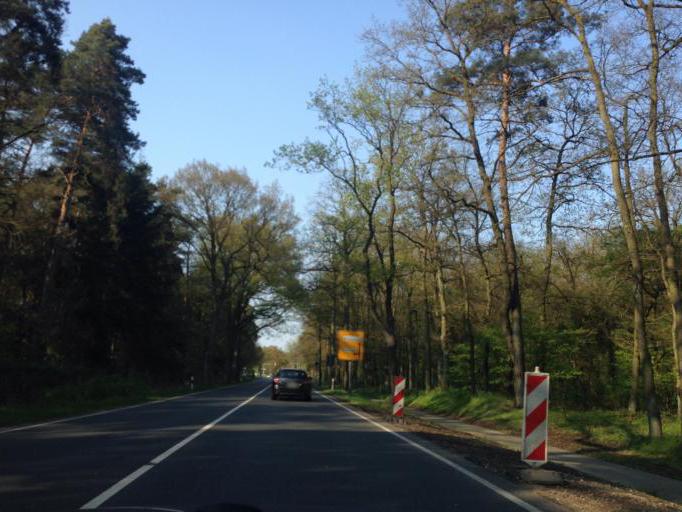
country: DE
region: Lower Saxony
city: Adelheidsdorf
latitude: 52.5872
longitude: 10.0667
